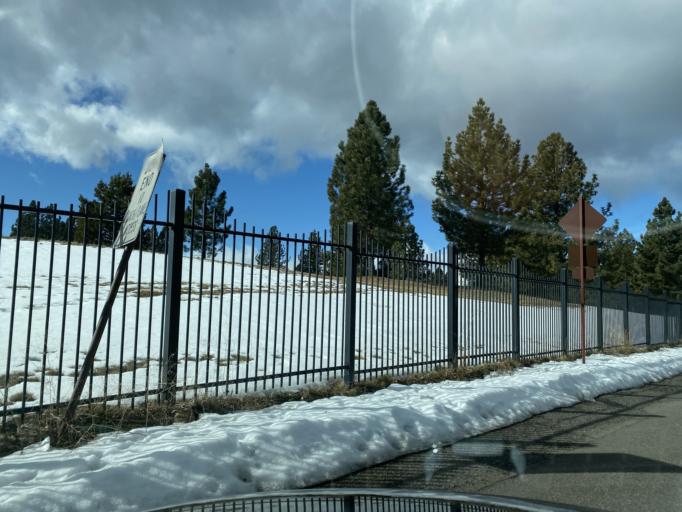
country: US
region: Nevada
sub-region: Douglas County
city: Kingsbury
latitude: 38.9690
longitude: -119.9377
